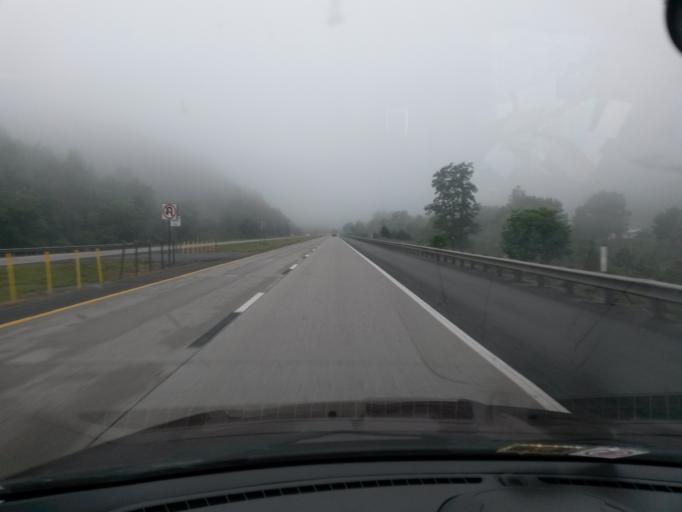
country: US
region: West Virginia
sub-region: Summers County
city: Hinton
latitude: 37.8148
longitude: -80.8139
